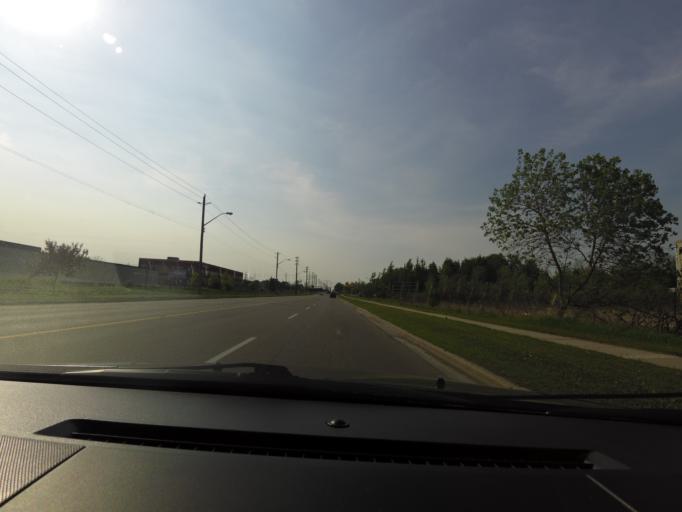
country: CA
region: Ontario
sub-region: Wellington County
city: Guelph
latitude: 43.5495
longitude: -80.2748
